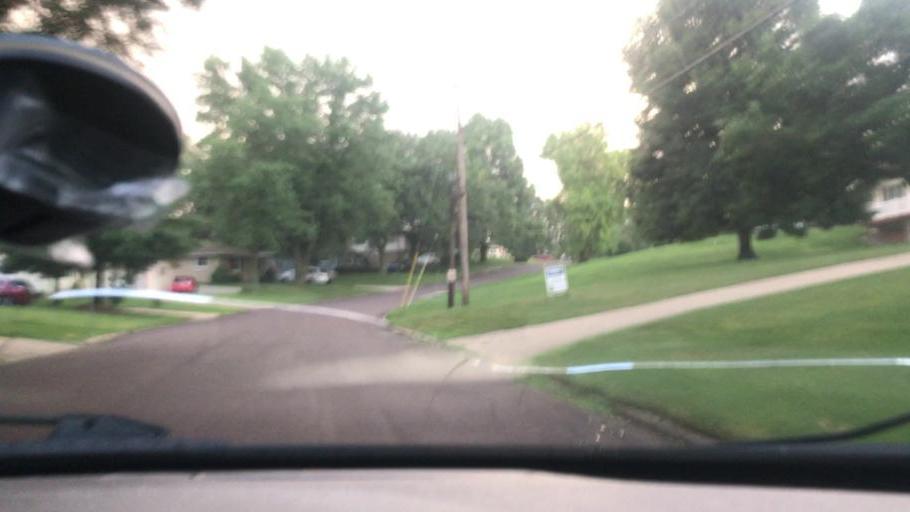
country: US
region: Illinois
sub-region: Tazewell County
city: Pekin
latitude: 40.5522
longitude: -89.6136
